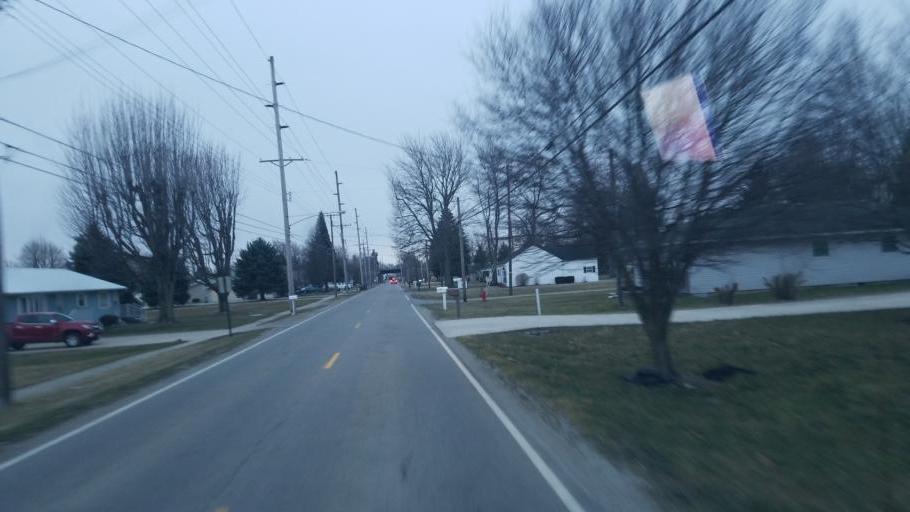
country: US
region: Ohio
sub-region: Defiance County
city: Hicksville
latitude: 41.3008
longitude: -84.7668
